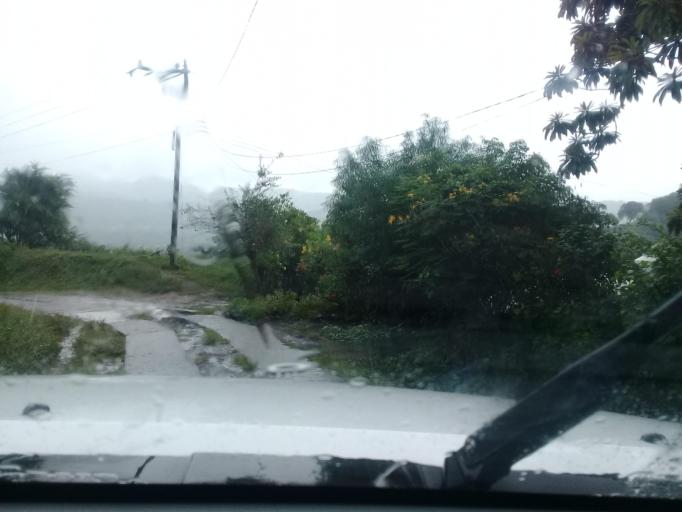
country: MX
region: Veracruz
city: Santiago Tuxtla
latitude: 18.4614
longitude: -95.3211
